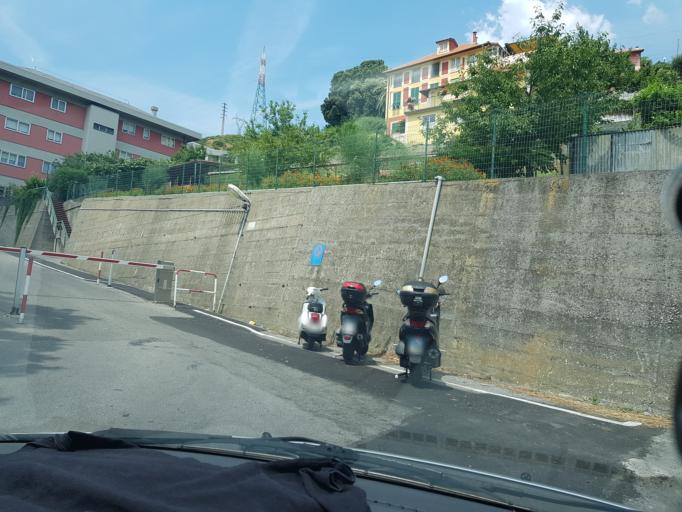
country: IT
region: Liguria
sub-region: Provincia di Genova
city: San Teodoro
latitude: 44.4369
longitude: 8.8713
